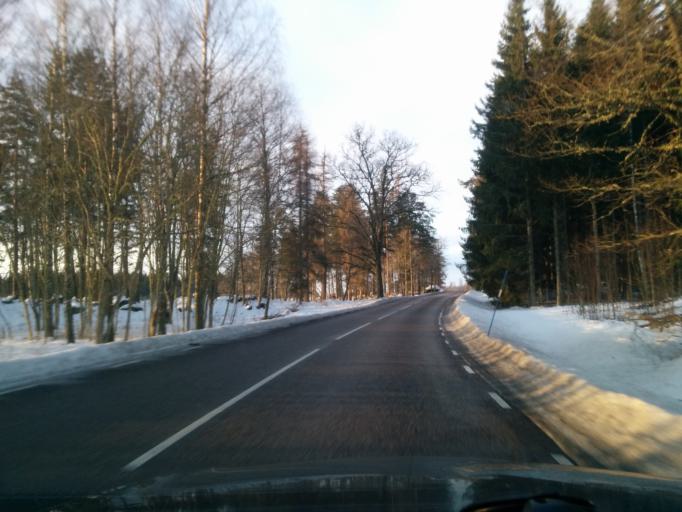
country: SE
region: Uppsala
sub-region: Tierps Kommun
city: Orbyhus
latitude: 60.1927
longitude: 17.6849
